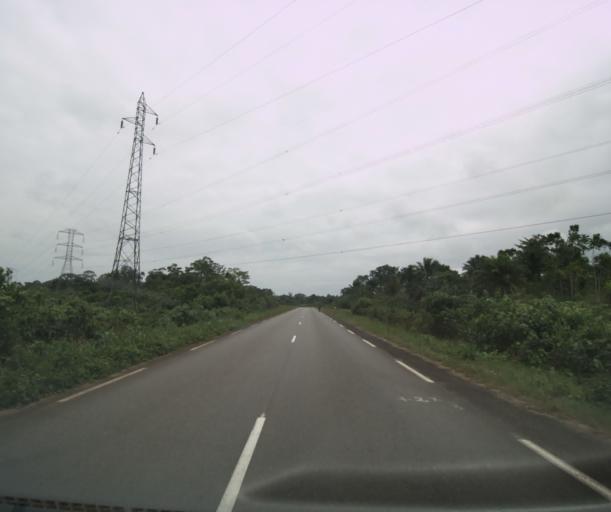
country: CM
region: South Province
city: Kribi
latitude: 3.1387
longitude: 10.0125
